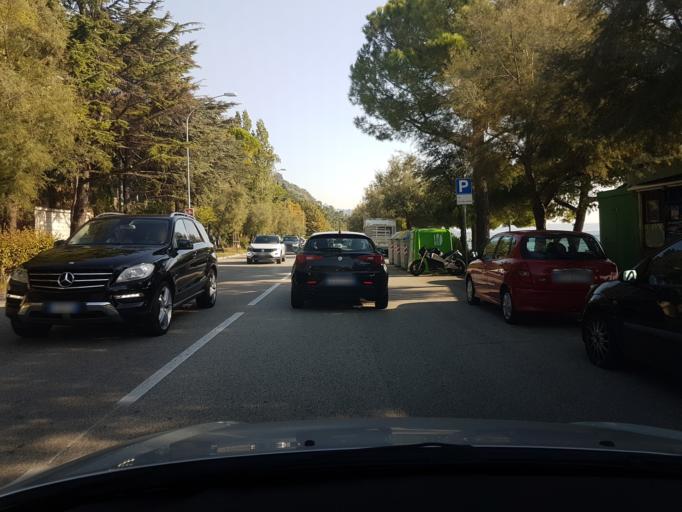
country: IT
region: Friuli Venezia Giulia
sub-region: Provincia di Trieste
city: Prosecco-Contovello
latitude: 45.6960
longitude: 13.7342
